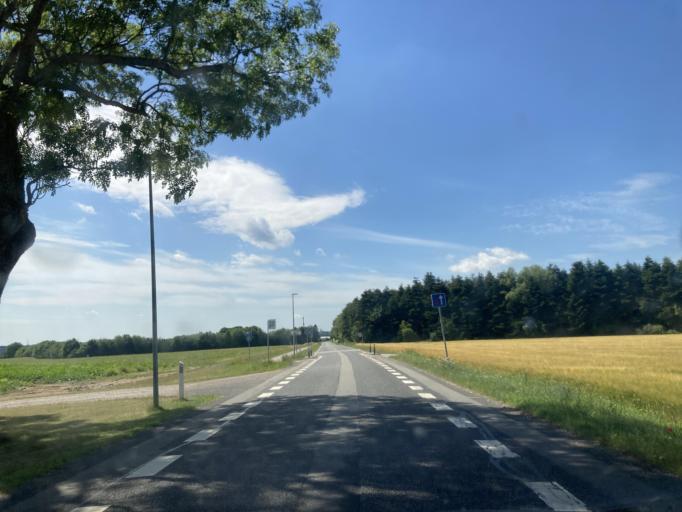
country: DK
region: Zealand
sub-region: Solrod Kommune
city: Solrod
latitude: 55.5217
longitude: 12.1602
